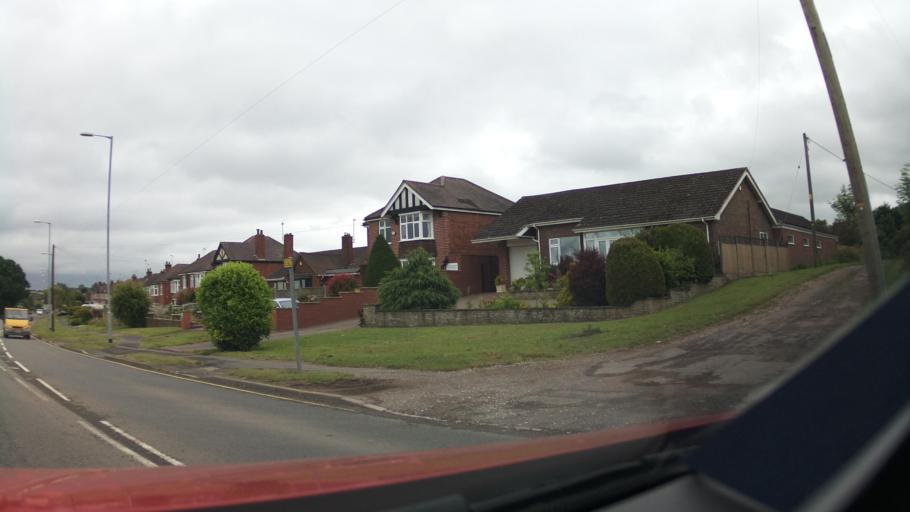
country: GB
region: England
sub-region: Staffordshire
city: Burton upon Trent
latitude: 52.8341
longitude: -1.6539
